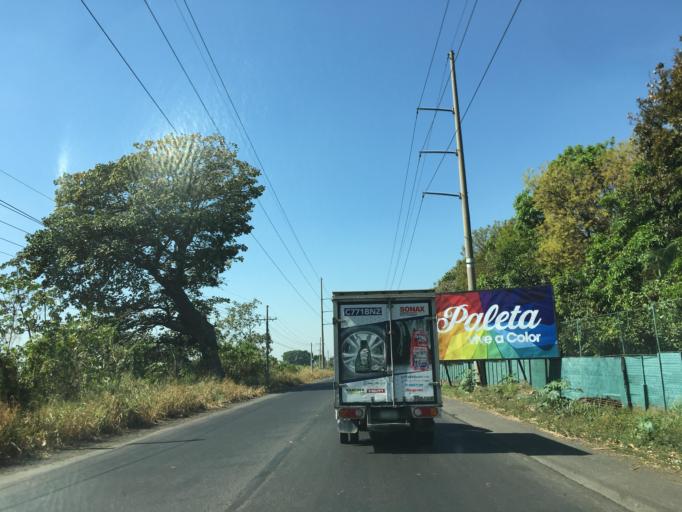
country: GT
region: Escuintla
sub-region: Municipio de Escuintla
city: Escuintla
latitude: 14.2551
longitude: -90.8015
